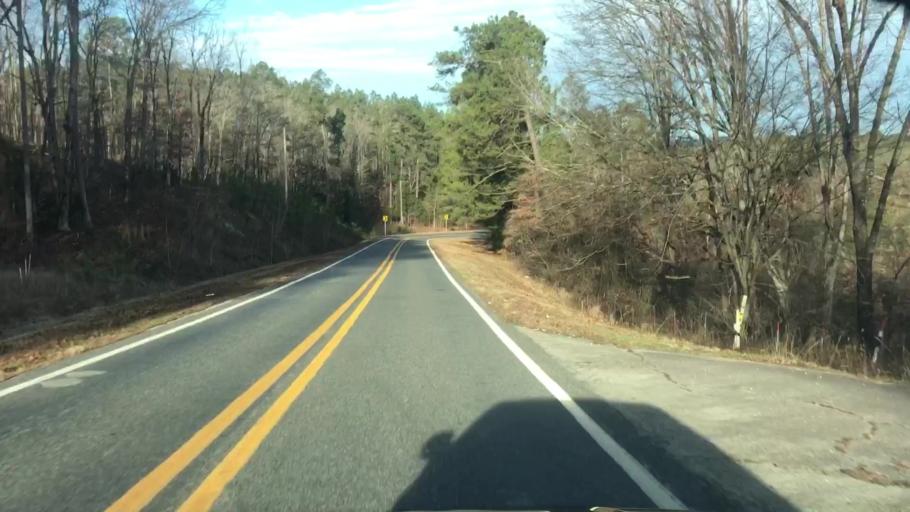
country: US
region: Arkansas
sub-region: Garland County
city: Rockwell
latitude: 34.4881
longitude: -93.2744
